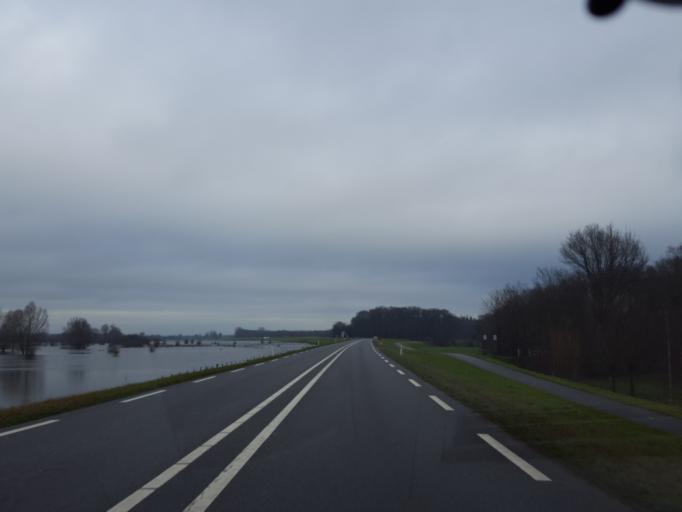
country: NL
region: Overijssel
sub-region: Gemeente Olst-Wijhe
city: Boskamp
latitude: 52.3000
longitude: 6.1117
